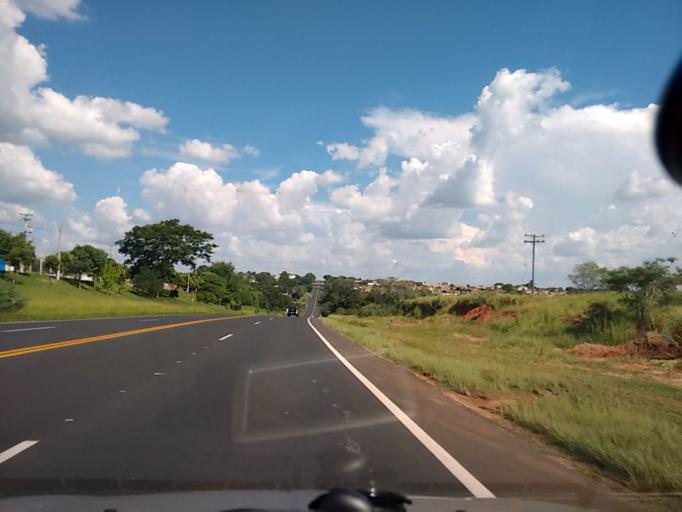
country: BR
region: Sao Paulo
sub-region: Pompeia
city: Pompeia
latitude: -22.1474
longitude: -50.0997
